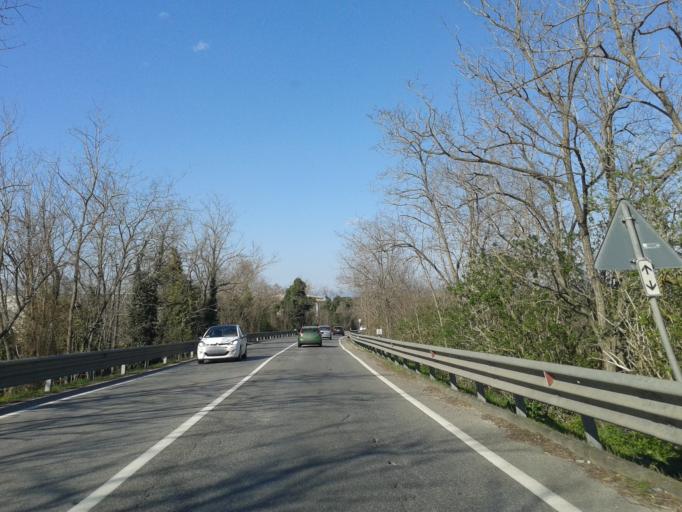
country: IT
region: Tuscany
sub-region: Province of Pisa
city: Marina di Pisa-Tirrenia-Calambrone
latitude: 43.6346
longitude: 10.3540
